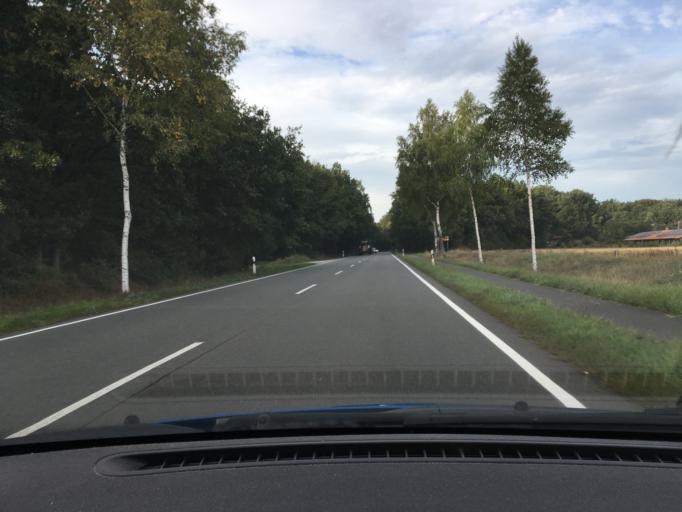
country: DE
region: Lower Saxony
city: Wietzendorf
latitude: 52.8975
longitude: 9.9184
